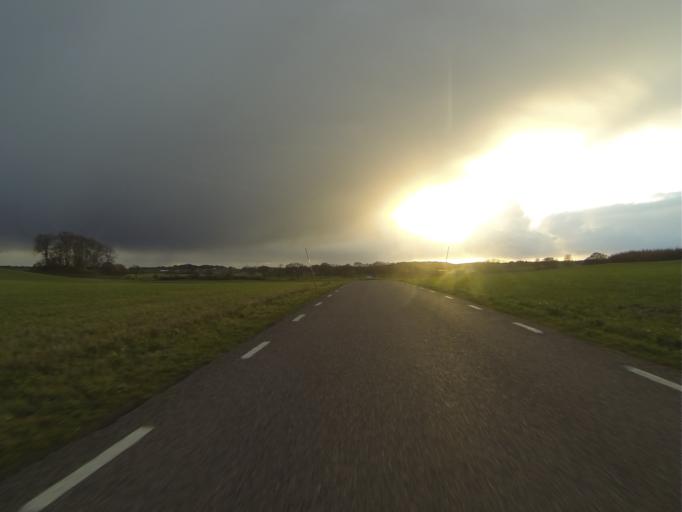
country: SE
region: Skane
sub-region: Lunds Kommun
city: Genarp
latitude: 55.5783
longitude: 13.3641
